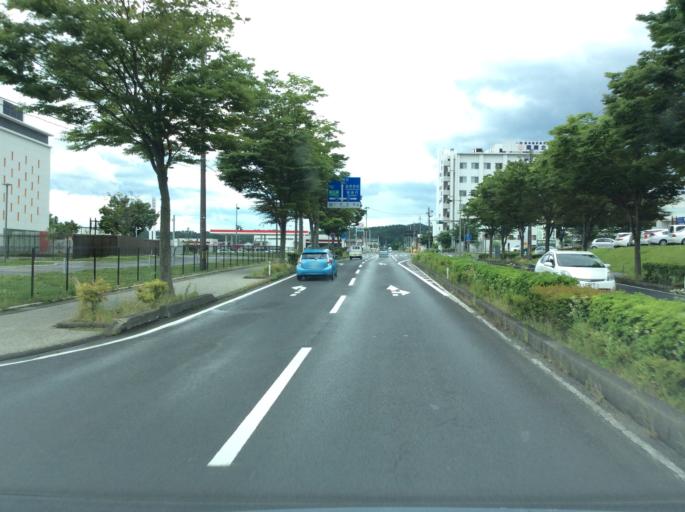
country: JP
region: Fukushima
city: Fukushima-shi
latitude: 37.7280
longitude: 140.3879
